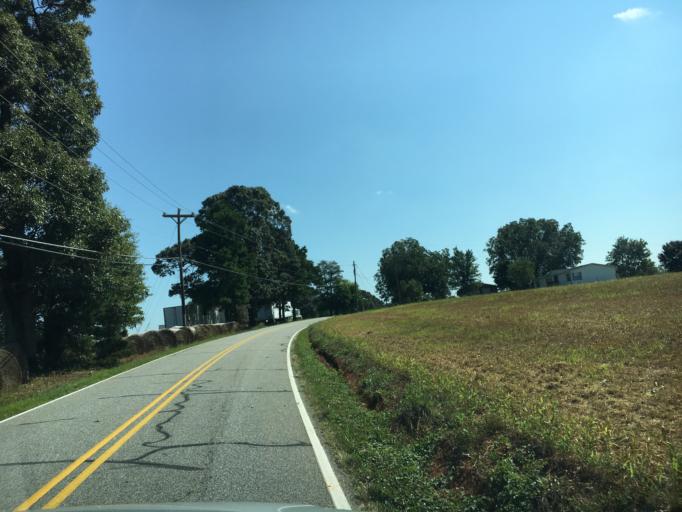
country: US
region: South Carolina
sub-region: Spartanburg County
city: Valley Falls
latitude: 35.0136
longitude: -81.9322
